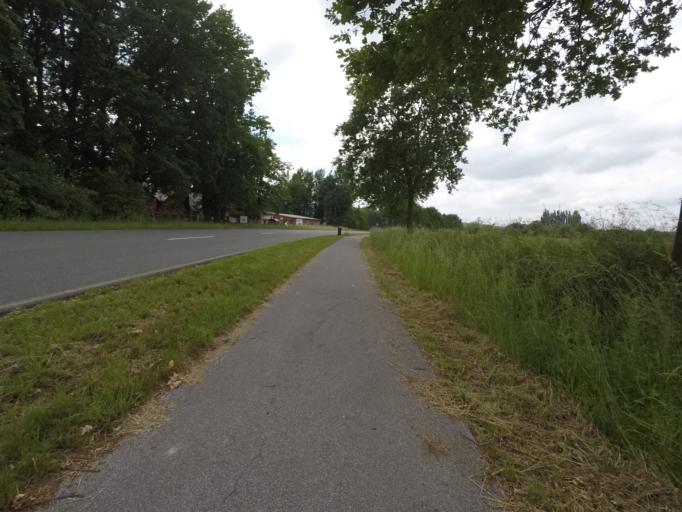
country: DE
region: North Rhine-Westphalia
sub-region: Regierungsbezirk Detmold
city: Werther
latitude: 52.1005
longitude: 8.3979
